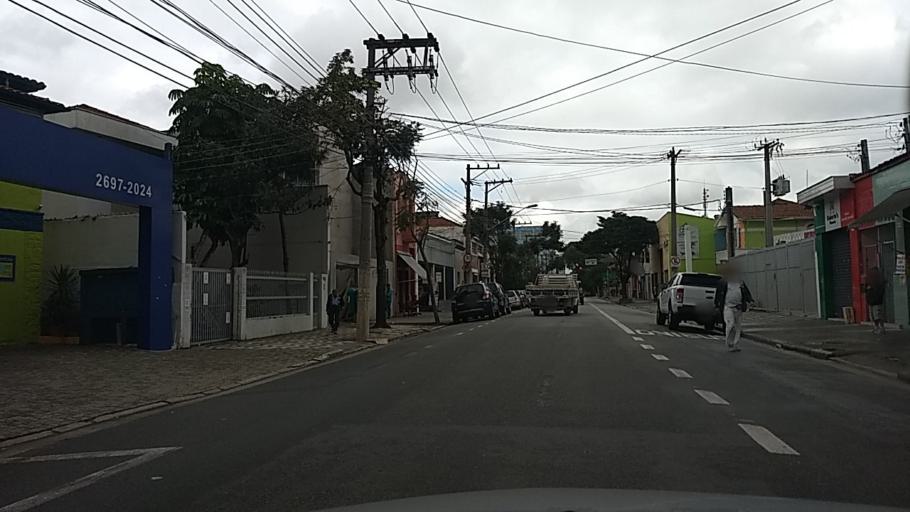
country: BR
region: Sao Paulo
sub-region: Sao Paulo
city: Sao Paulo
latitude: -23.5407
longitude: -46.5951
